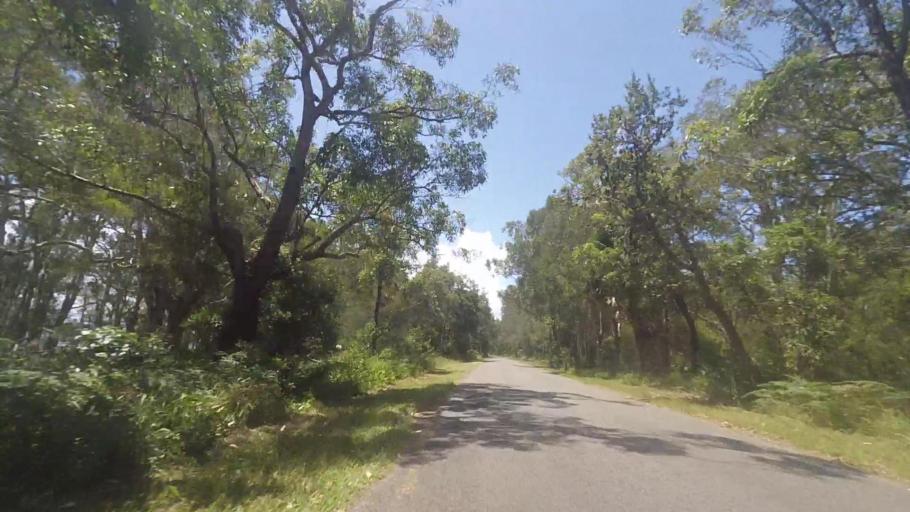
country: AU
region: New South Wales
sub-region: Great Lakes
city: Bulahdelah
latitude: -32.5322
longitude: 152.3216
